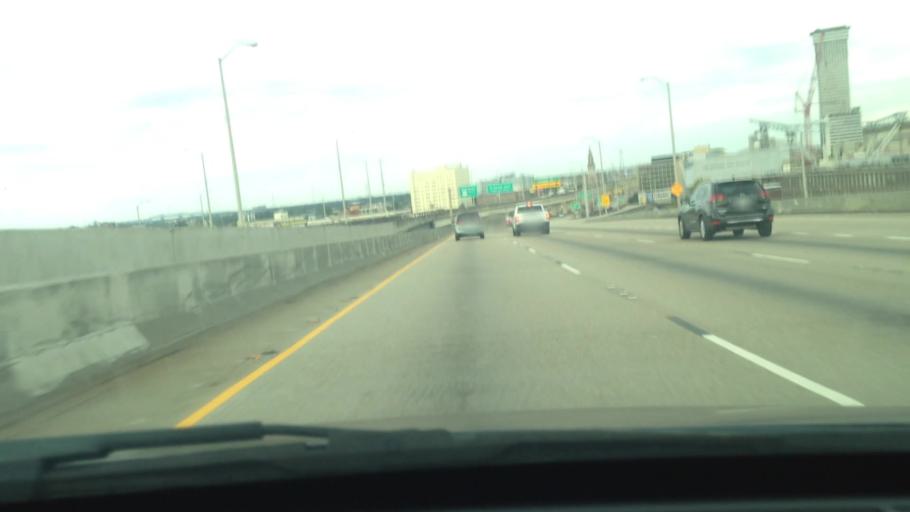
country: US
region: Louisiana
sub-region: Orleans Parish
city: New Orleans
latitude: 29.9392
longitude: -90.0666
